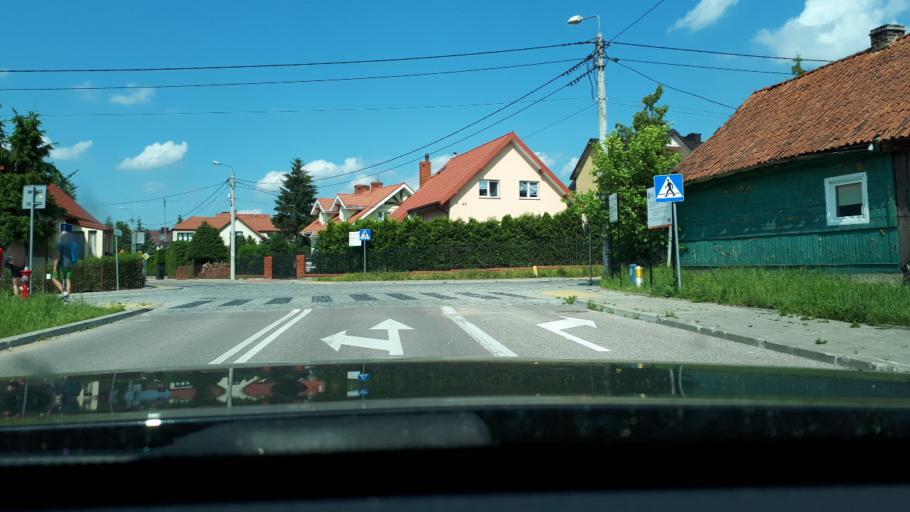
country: PL
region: Podlasie
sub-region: Powiat bialostocki
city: Choroszcz
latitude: 53.1454
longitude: 22.9841
